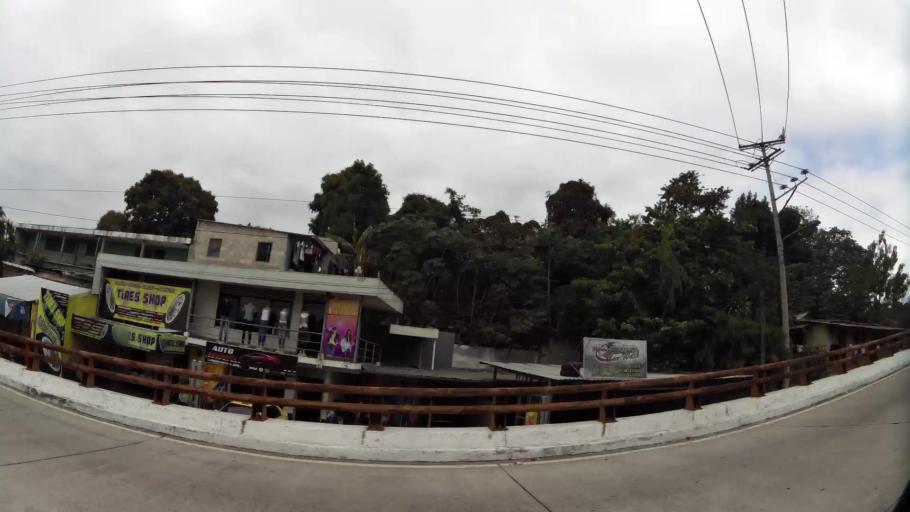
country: SV
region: San Salvador
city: Mejicanos
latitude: 13.7168
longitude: -89.2305
